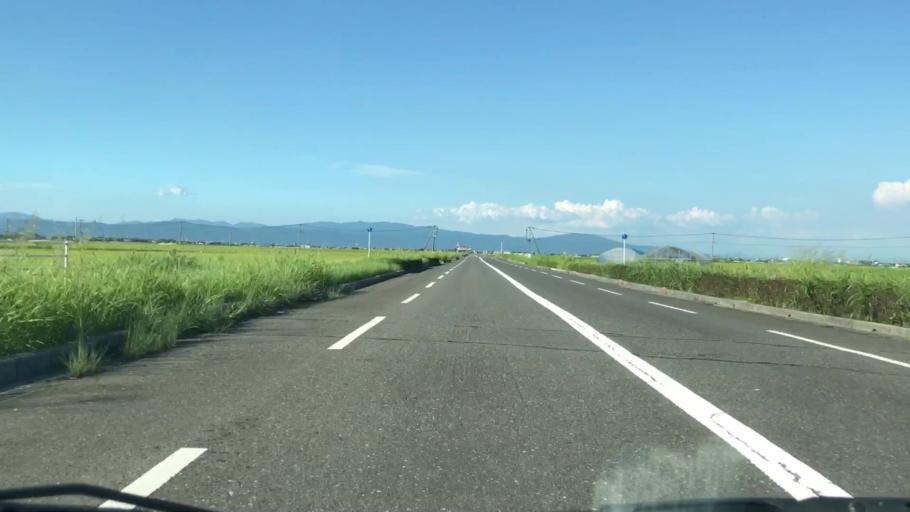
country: JP
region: Saga Prefecture
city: Okawa
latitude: 33.1698
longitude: 130.2943
